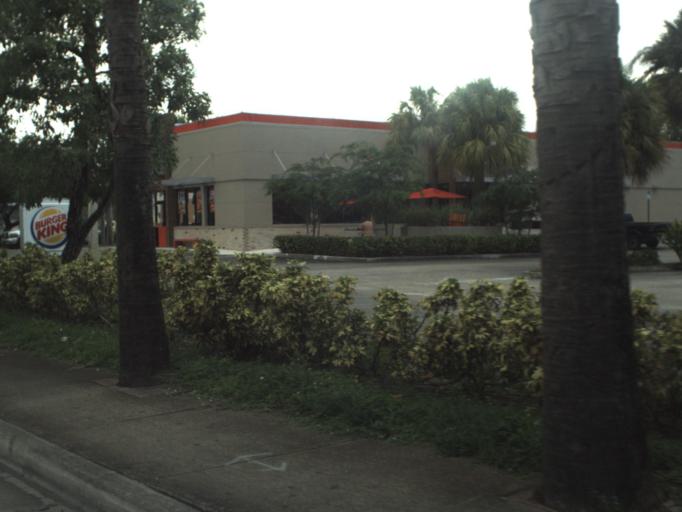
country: US
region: Florida
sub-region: Miami-Dade County
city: Golden Glades
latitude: 25.9284
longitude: -80.1957
